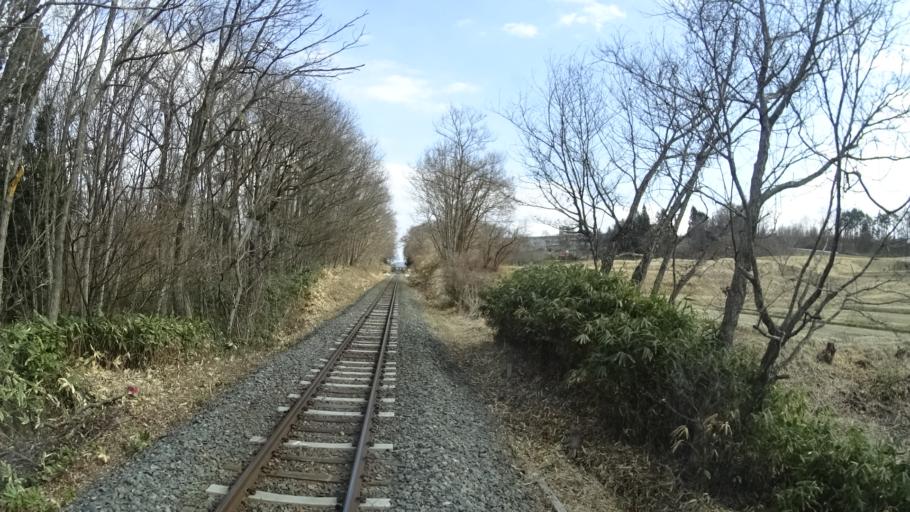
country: JP
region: Iwate
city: Hanamaki
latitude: 39.3928
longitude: 141.2151
